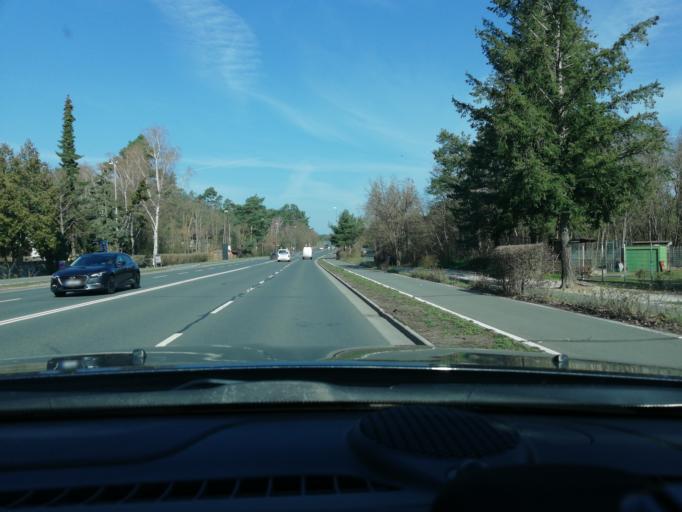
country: DE
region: Bavaria
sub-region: Regierungsbezirk Mittelfranken
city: Mohrendorf
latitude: 49.6098
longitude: 10.9792
